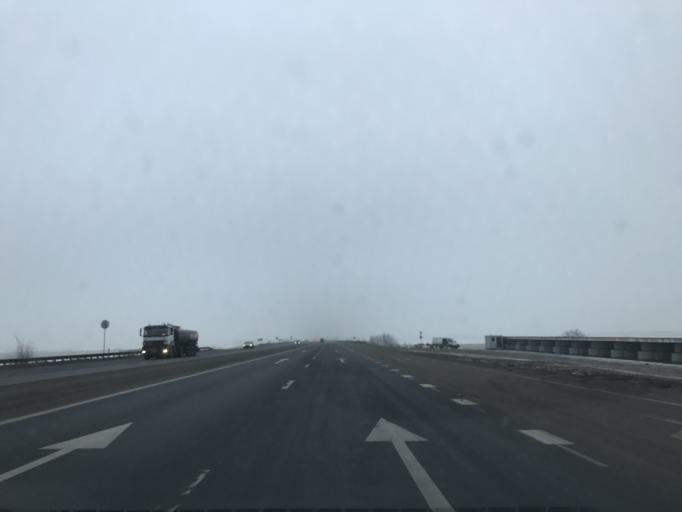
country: RU
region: Rostov
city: Grushevskaya
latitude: 47.4471
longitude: 39.9743
